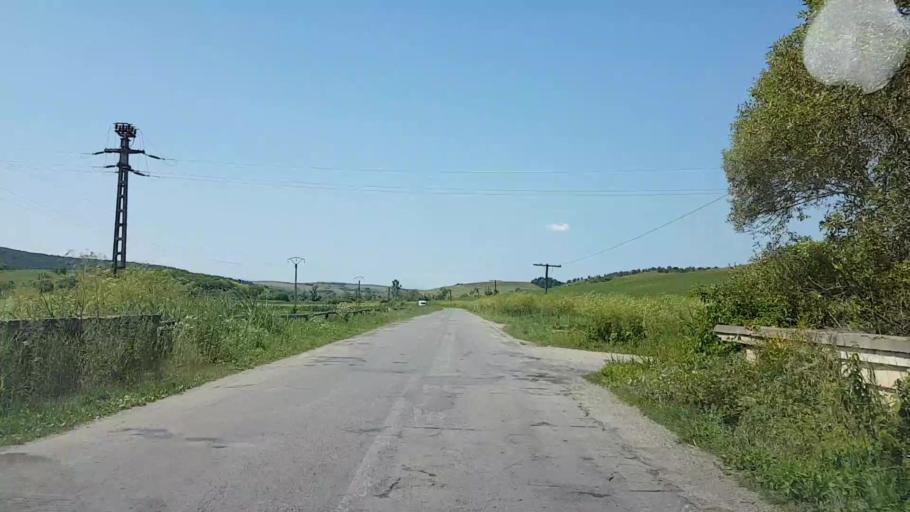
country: RO
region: Sibiu
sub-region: Oras Agnita
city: Ruja
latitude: 46.0116
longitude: 24.6850
